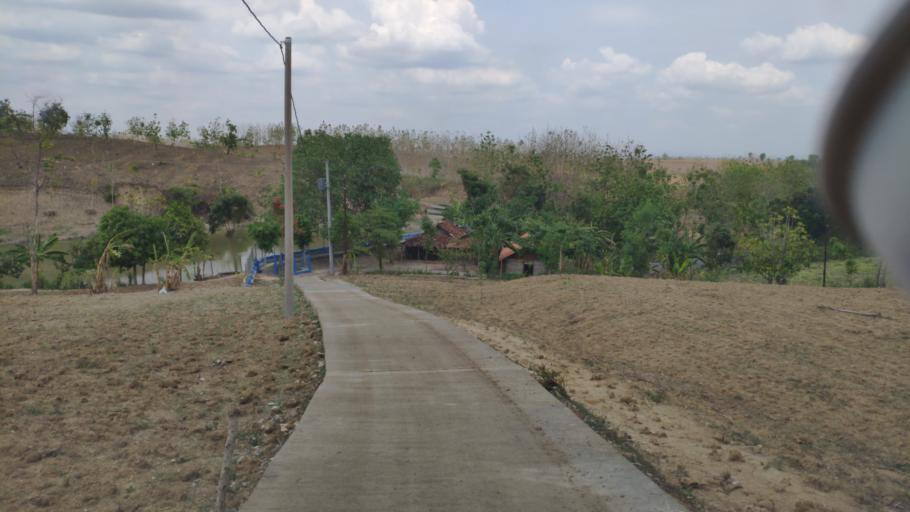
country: ID
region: Central Java
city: Gumiring
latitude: -7.0506
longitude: 111.3961
